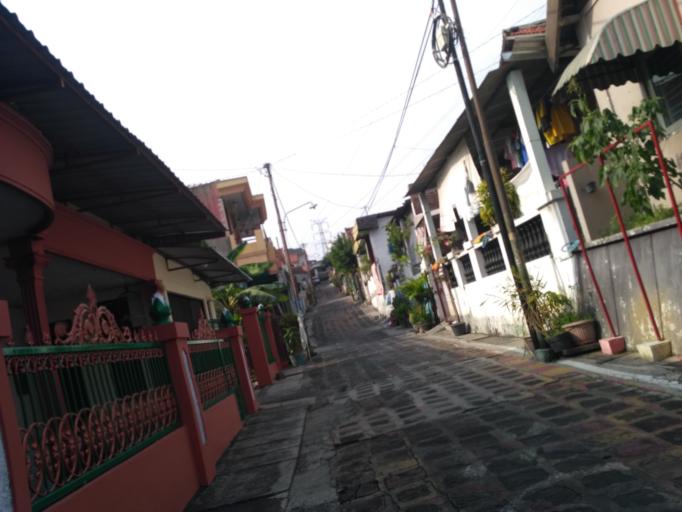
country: ID
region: Central Java
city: Semarang
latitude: -7.0137
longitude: 110.4452
